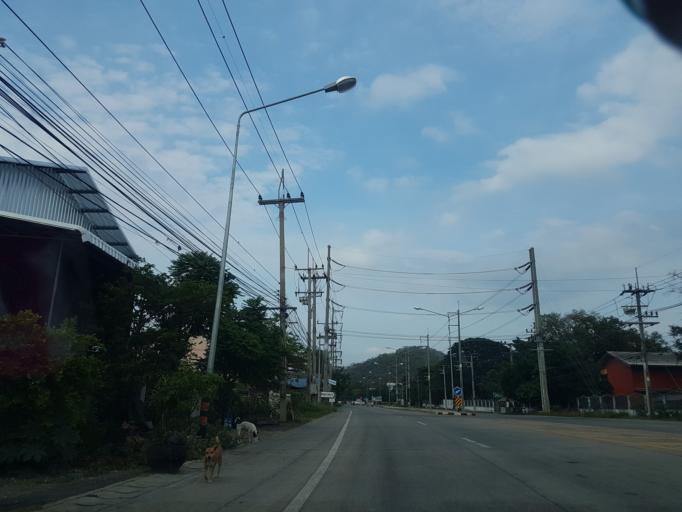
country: TH
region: Sara Buri
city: Phra Phutthabat
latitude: 14.7206
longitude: 100.8020
